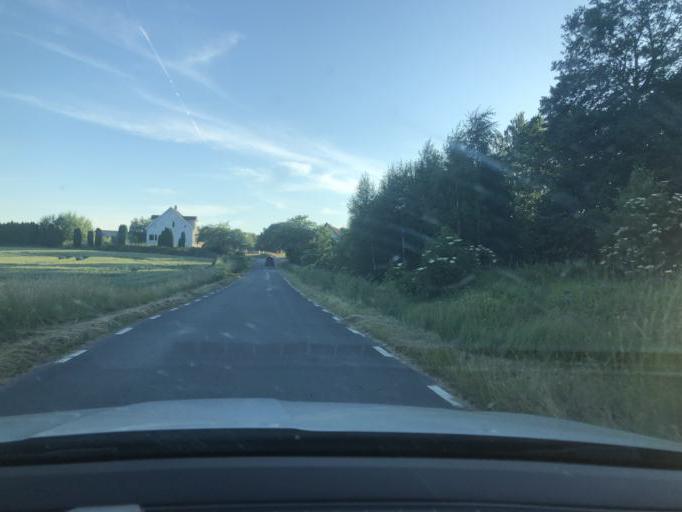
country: SE
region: Blekinge
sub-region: Karlshamns Kommun
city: Morrum
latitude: 56.1409
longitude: 14.6508
